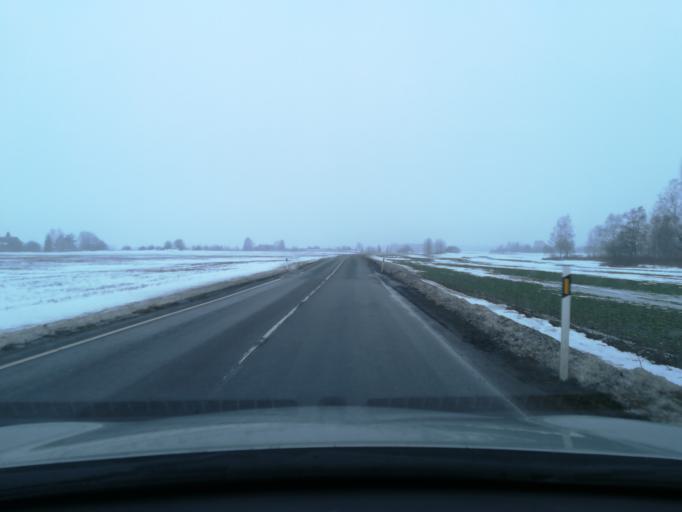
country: EE
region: Harju
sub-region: Raasiku vald
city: Raasiku
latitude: 59.3532
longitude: 25.1452
